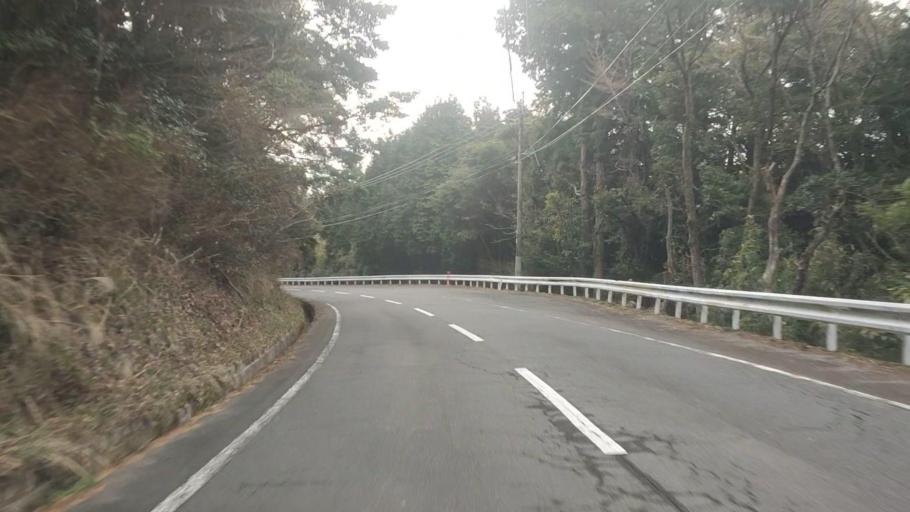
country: JP
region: Nagasaki
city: Shimabara
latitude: 32.7241
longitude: 130.2501
